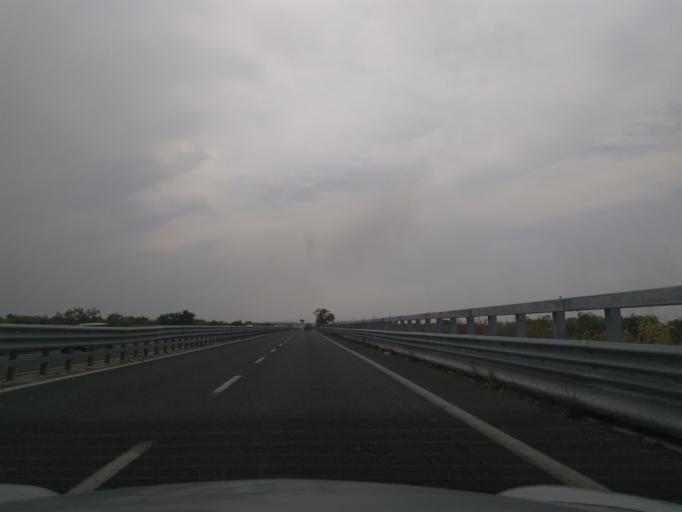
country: IT
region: Apulia
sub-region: Provincia di Bari
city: Giovinazzo
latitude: 41.1707
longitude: 16.6962
